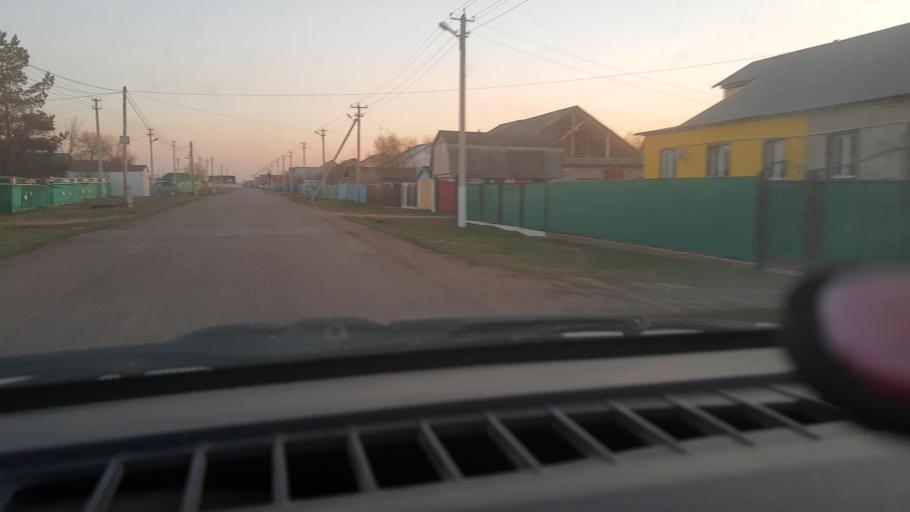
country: RU
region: Bashkortostan
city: Asanovo
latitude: 54.9080
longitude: 55.4881
